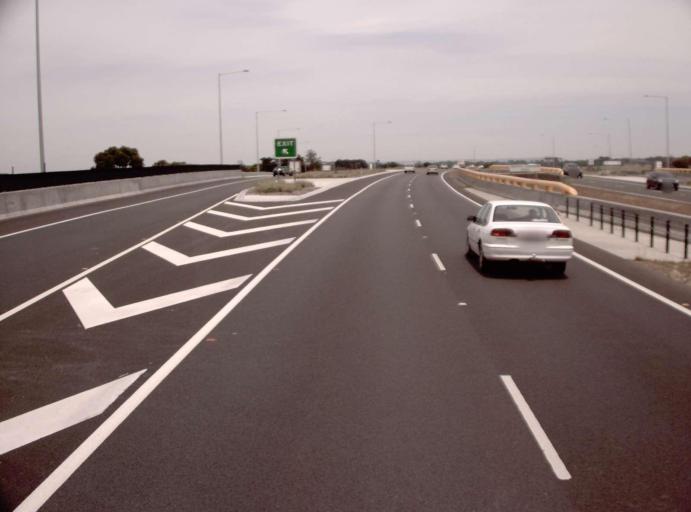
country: AU
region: Victoria
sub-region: Mornington Peninsula
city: Baxter
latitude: -38.1939
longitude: 145.1532
